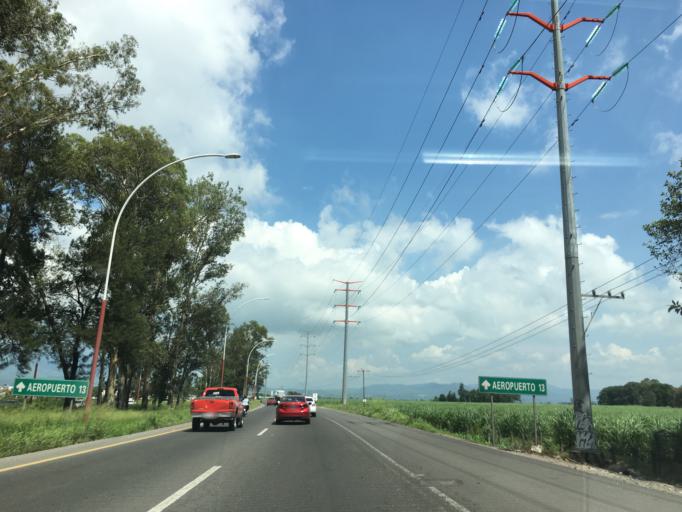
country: MX
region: Nayarit
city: Xalisco
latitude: 21.4683
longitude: -104.8853
